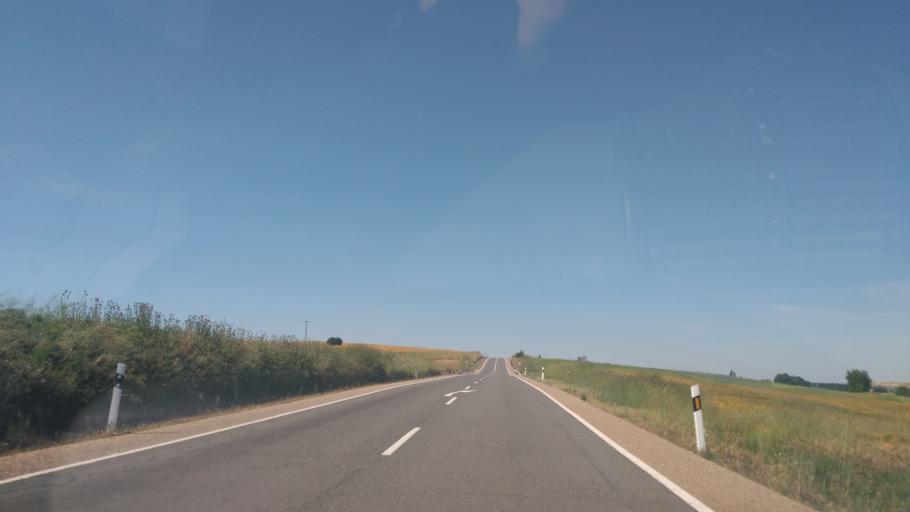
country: ES
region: Castille and Leon
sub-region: Provincia de Zamora
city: Corrales
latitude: 41.3339
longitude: -5.7323
